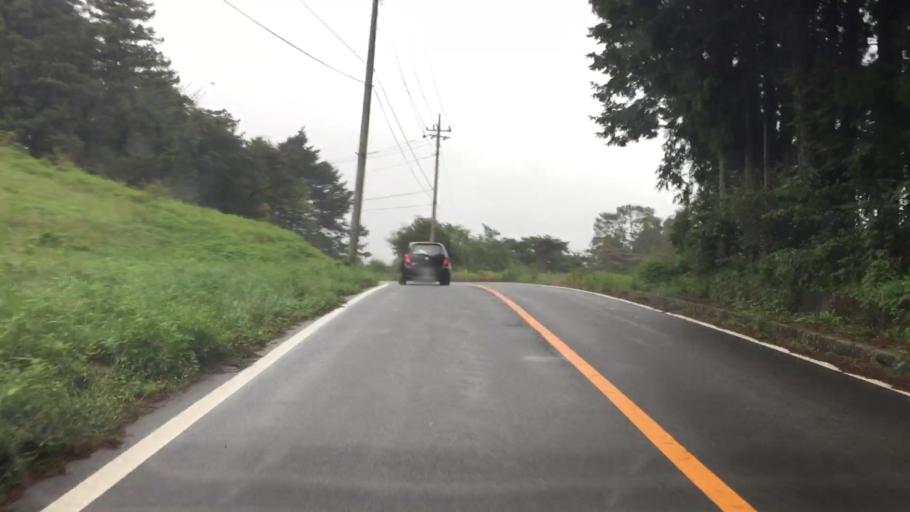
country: JP
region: Yamanashi
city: Fujikawaguchiko
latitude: 35.4015
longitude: 138.6121
